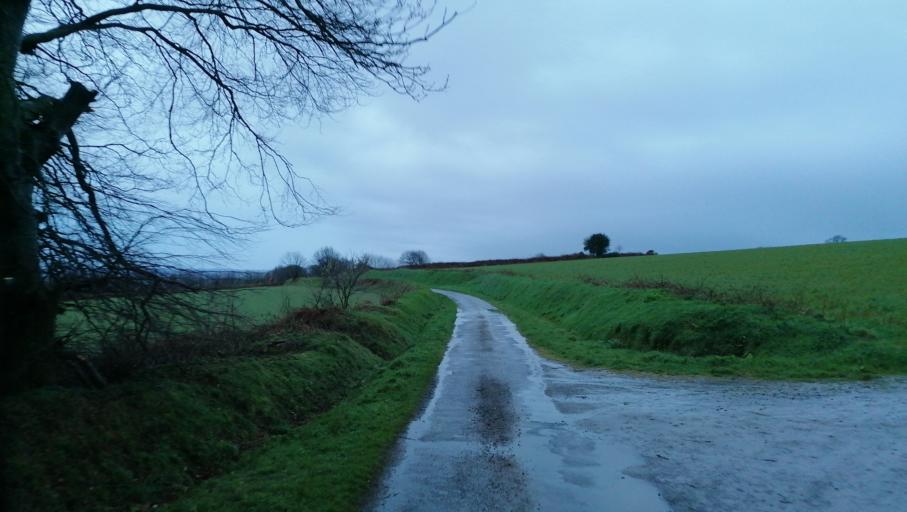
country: FR
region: Brittany
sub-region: Departement des Cotes-d'Armor
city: Plouagat
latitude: 48.4853
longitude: -2.9881
